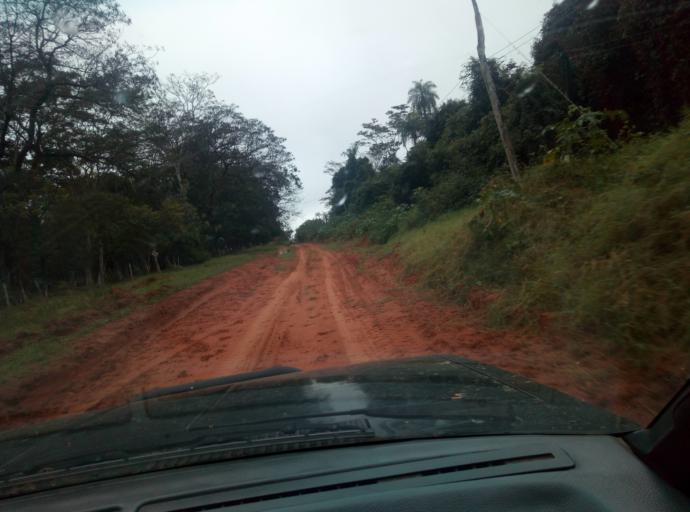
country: PY
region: Caaguazu
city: Carayao
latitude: -25.1919
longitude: -56.3412
